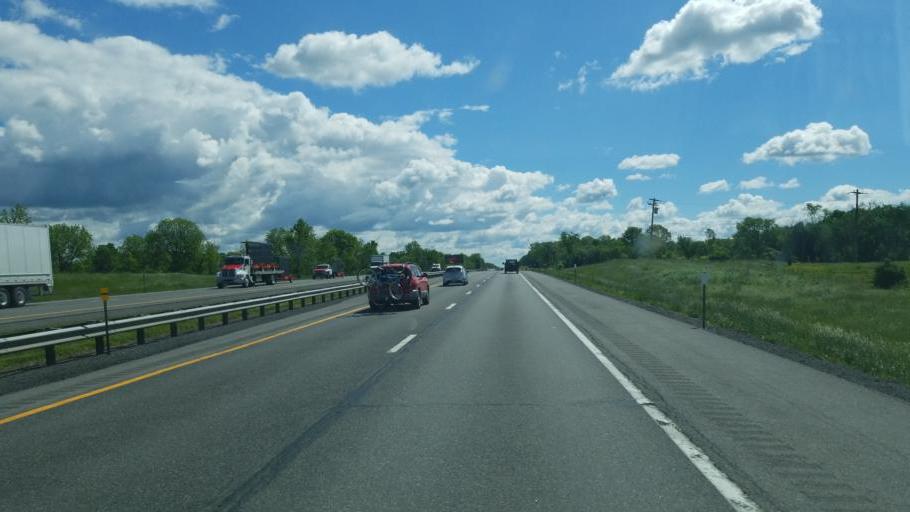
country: US
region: New York
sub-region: Oneida County
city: Vernon
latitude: 43.1287
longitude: -75.5427
